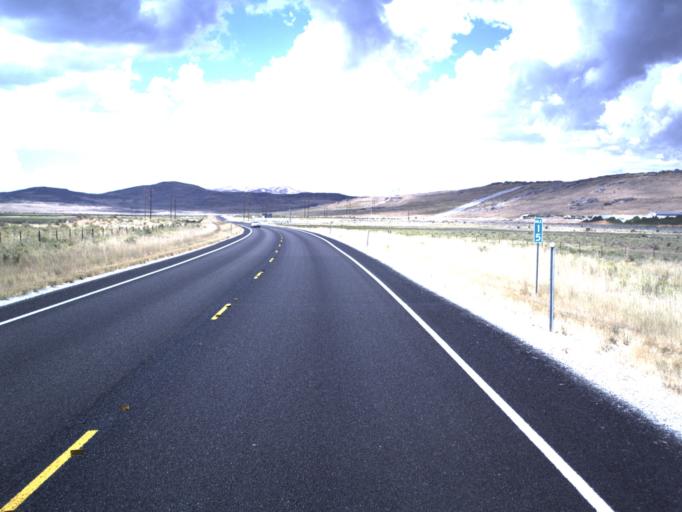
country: US
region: Utah
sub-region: Box Elder County
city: Tremonton
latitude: 41.6268
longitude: -112.3984
